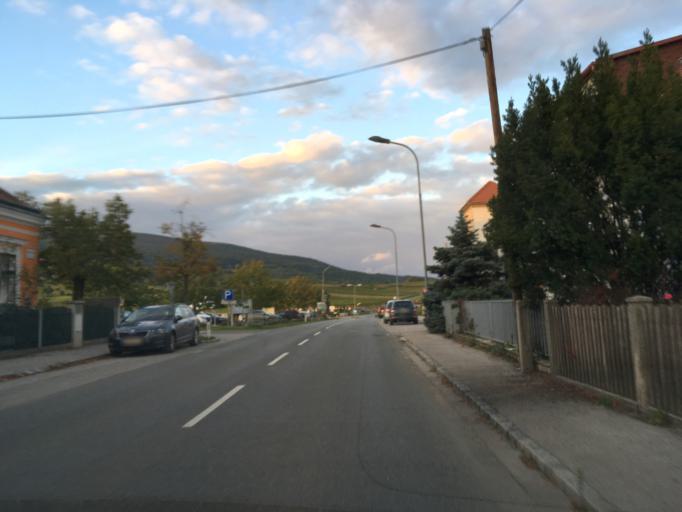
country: AT
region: Lower Austria
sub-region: Politischer Bezirk Baden
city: Pfaffstatten
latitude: 48.0197
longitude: 16.2570
